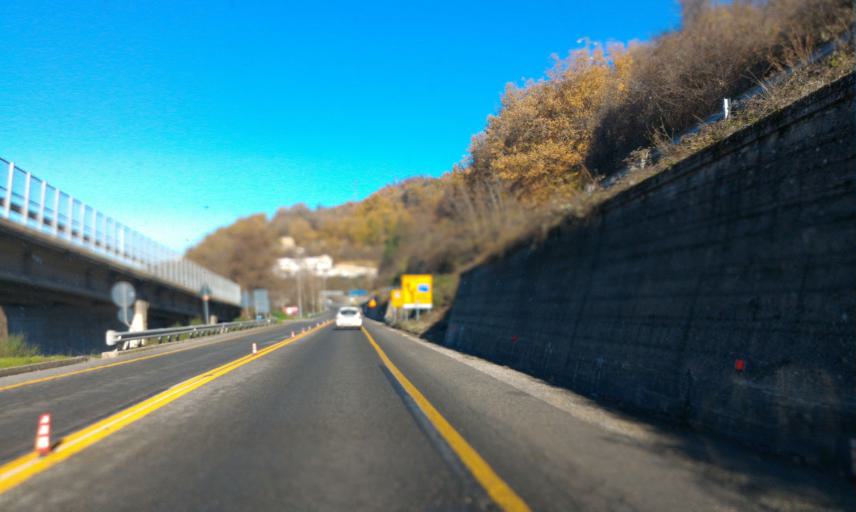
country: IT
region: Calabria
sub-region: Provincia di Cosenza
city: Spezzano Piccolo
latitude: 39.2939
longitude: 16.3450
